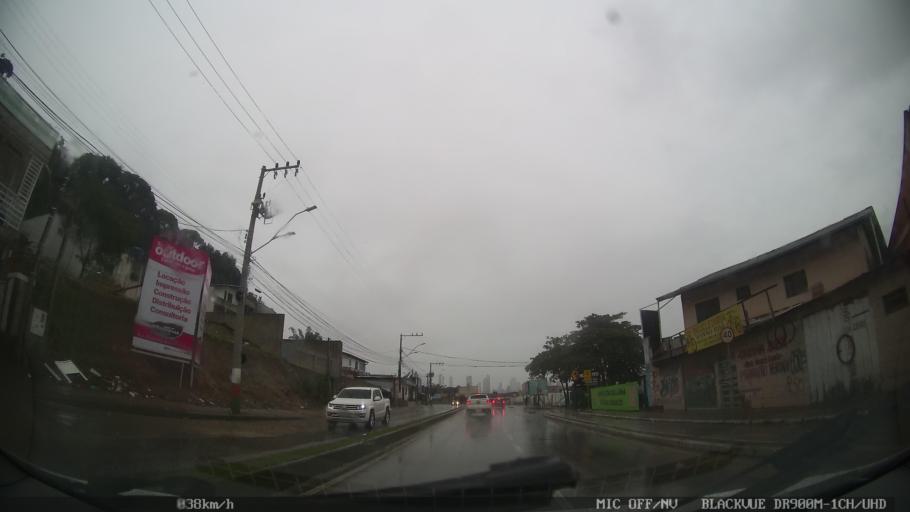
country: BR
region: Santa Catarina
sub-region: Balneario Camboriu
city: Balneario Camboriu
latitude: -27.0073
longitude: -48.6484
